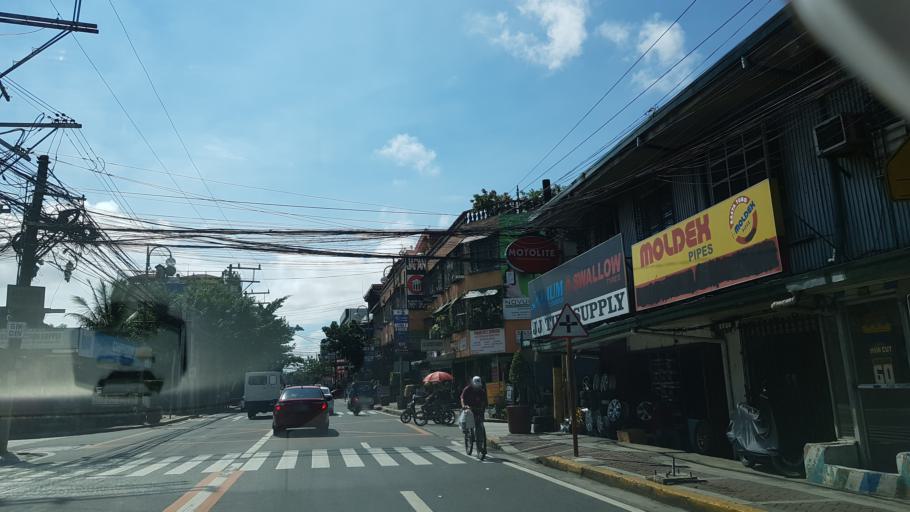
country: PH
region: Metro Manila
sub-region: Makati City
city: Makati City
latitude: 14.5700
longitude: 121.0235
